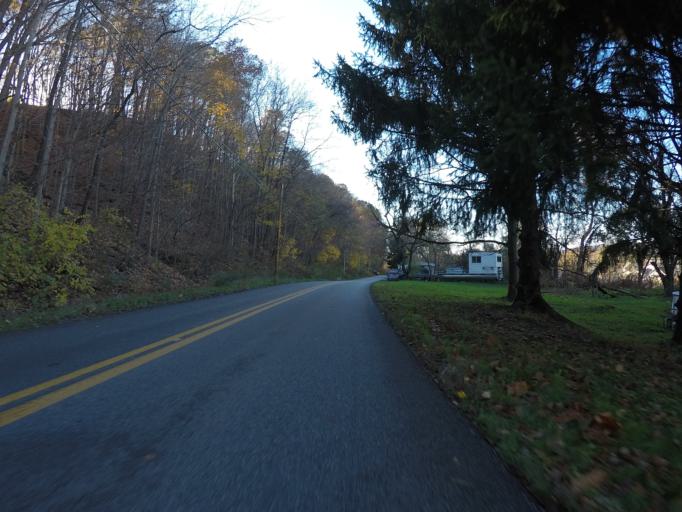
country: US
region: Ohio
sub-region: Lawrence County
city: Burlington
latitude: 38.3957
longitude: -82.5227
